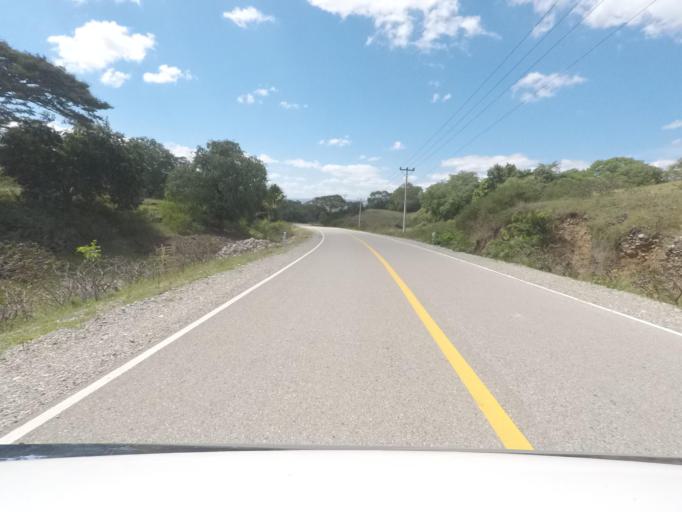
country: TL
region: Lautem
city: Lospalos
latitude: -8.4037
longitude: 126.8230
